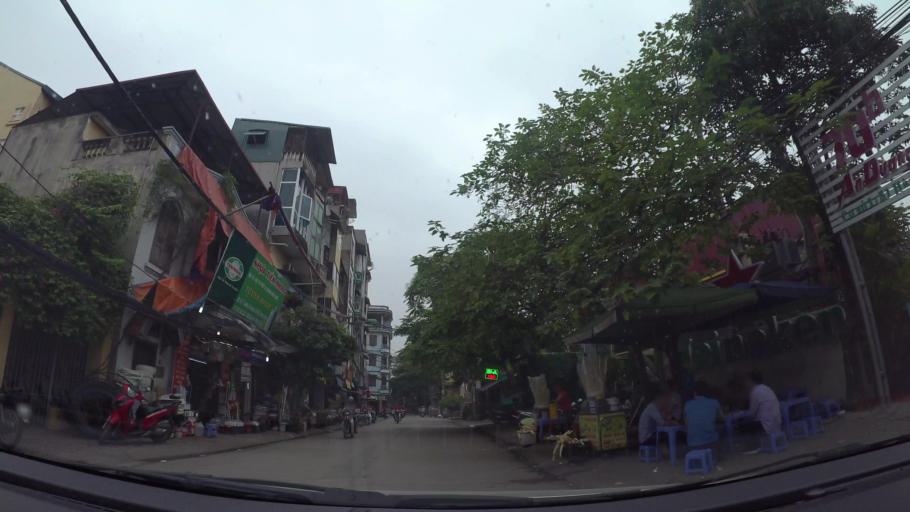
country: VN
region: Ha Noi
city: Hoan Kiem
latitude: 21.0540
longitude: 105.8404
